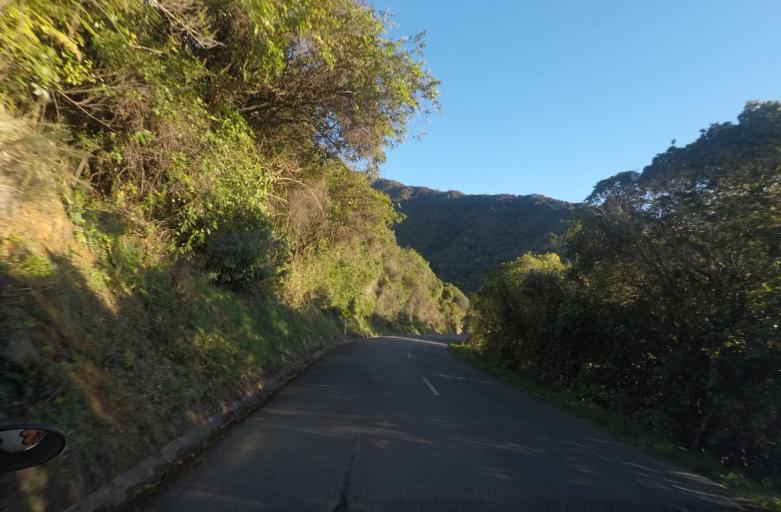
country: NZ
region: Marlborough
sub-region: Marlborough District
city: Picton
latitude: -41.2697
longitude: 173.9430
